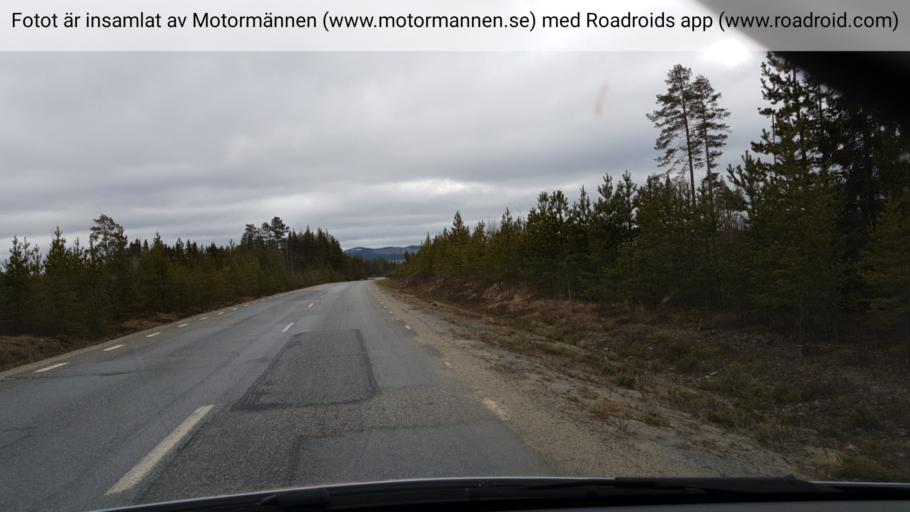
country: SE
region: Vaesterbotten
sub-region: Lycksele Kommun
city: Lycksele
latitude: 63.9867
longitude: 18.4806
